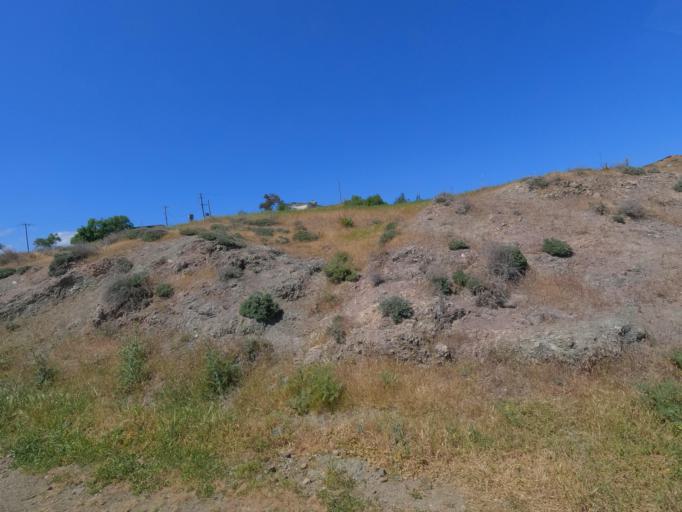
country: CY
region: Lefkosia
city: Peristerona
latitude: 35.0550
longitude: 33.0722
